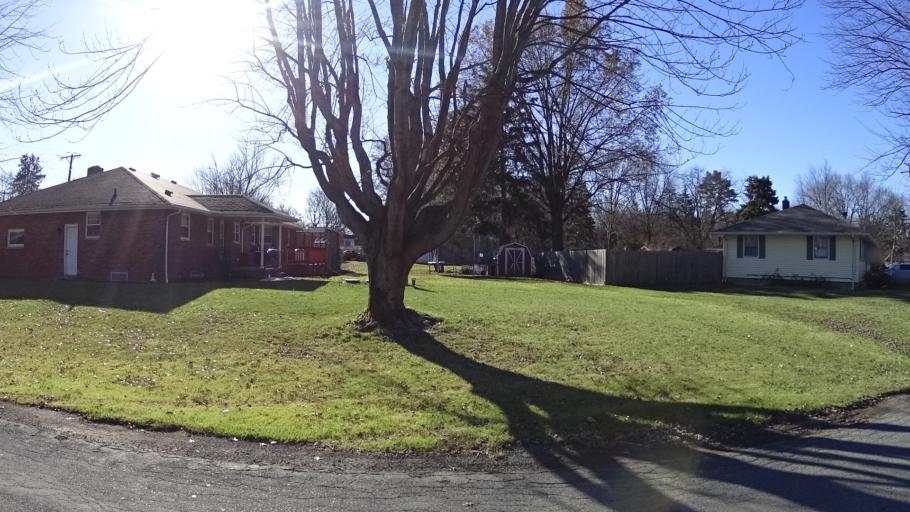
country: US
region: Ohio
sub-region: Lorain County
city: Elyria
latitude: 41.3991
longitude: -82.1502
